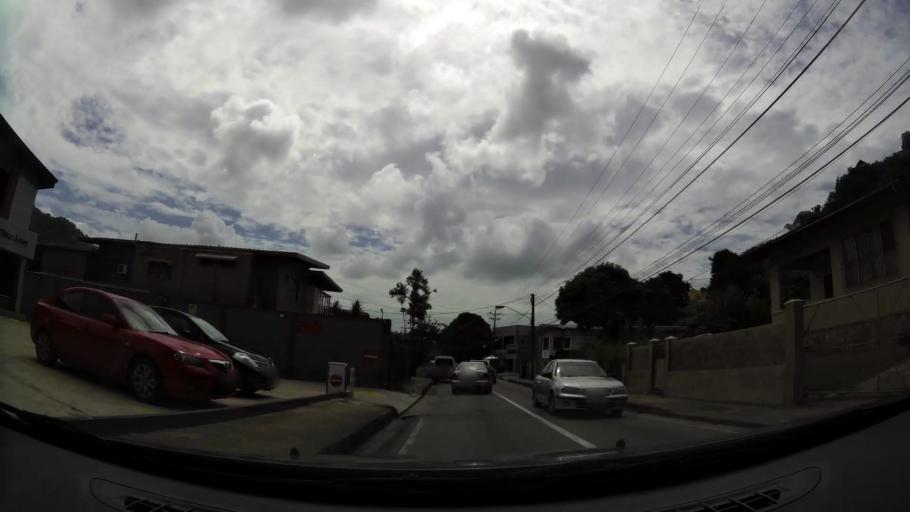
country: TT
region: Diego Martin
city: Petit Valley
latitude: 10.6959
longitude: -61.5564
